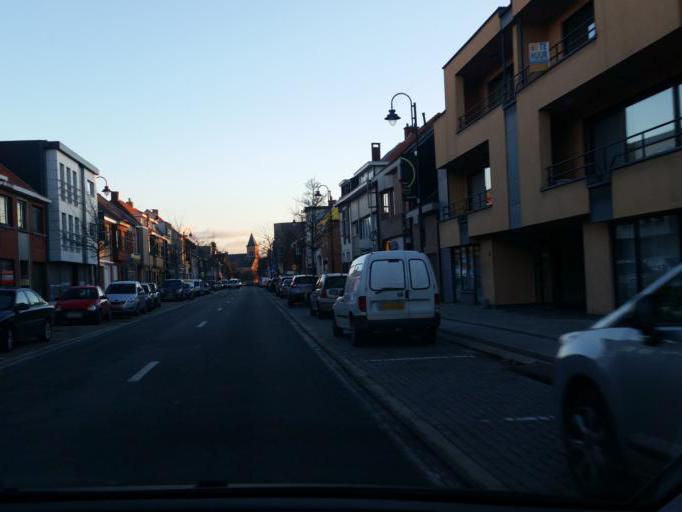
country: BE
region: Flanders
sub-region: Provincie Oost-Vlaanderen
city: Sint-Gillis-Waas
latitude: 51.2925
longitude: 4.1731
